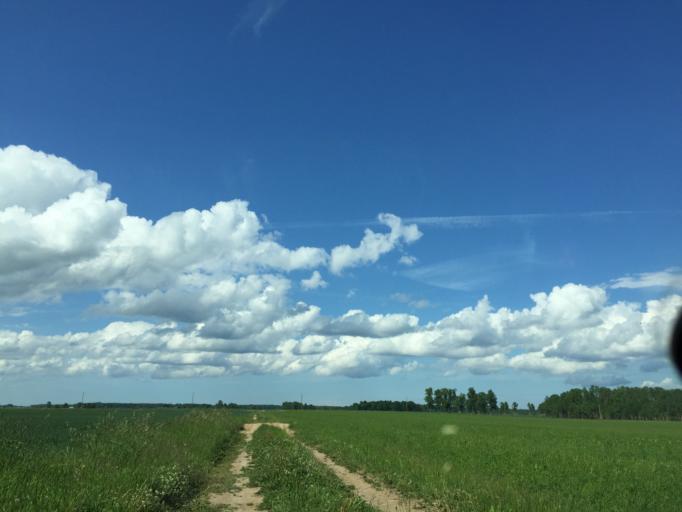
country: LV
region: Dobeles Rajons
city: Dobele
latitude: 56.6832
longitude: 23.4000
